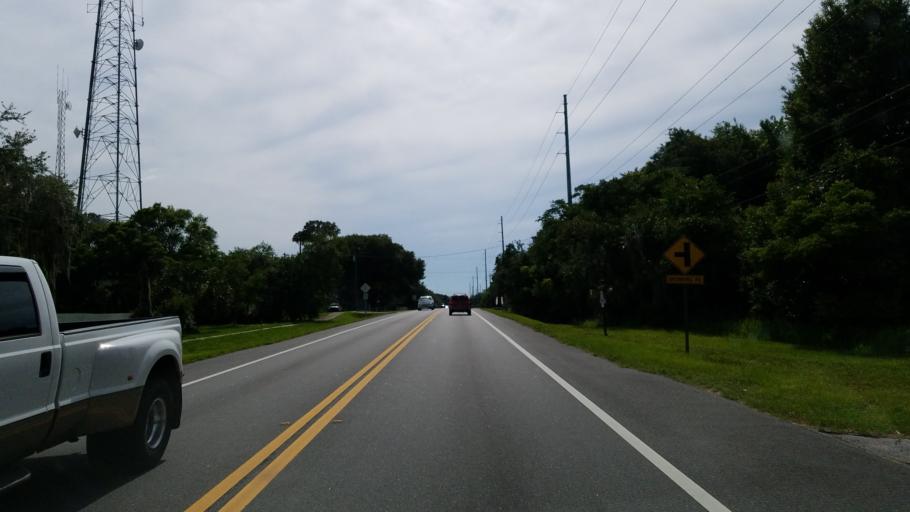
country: US
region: Florida
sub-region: Hillsborough County
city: Fish Hawk
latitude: 27.8501
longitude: -82.1726
